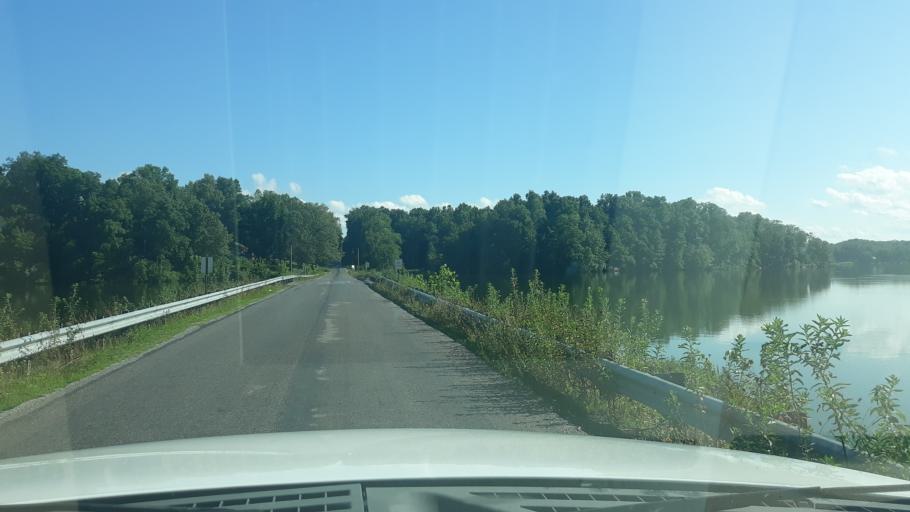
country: US
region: Illinois
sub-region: Saline County
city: Harrisburg
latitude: 37.8550
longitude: -88.5814
